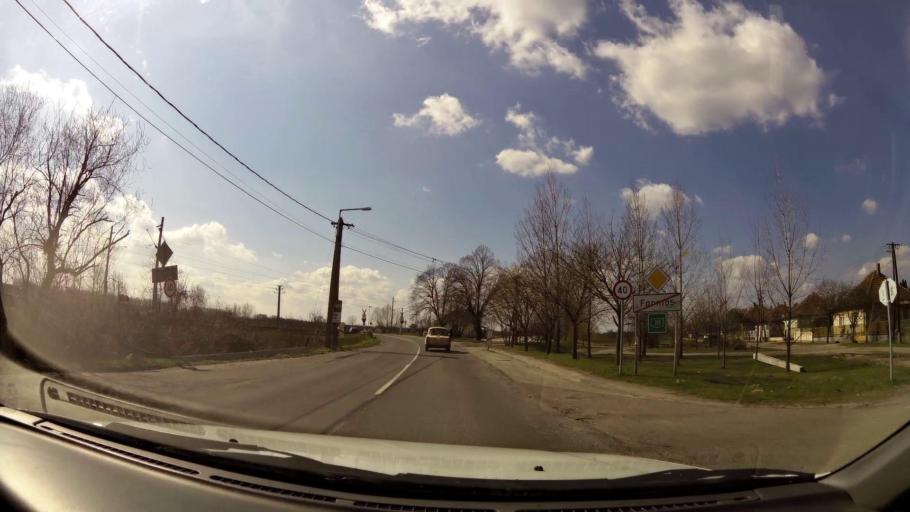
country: HU
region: Pest
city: Farmos
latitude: 47.3553
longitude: 19.8389
